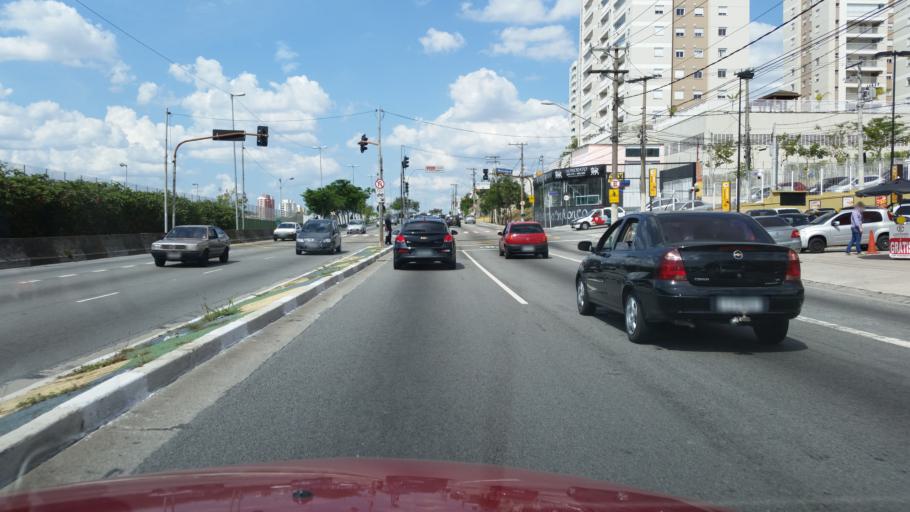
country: BR
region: Sao Paulo
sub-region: Guarulhos
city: Guarulhos
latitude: -23.5325
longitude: -46.5361
